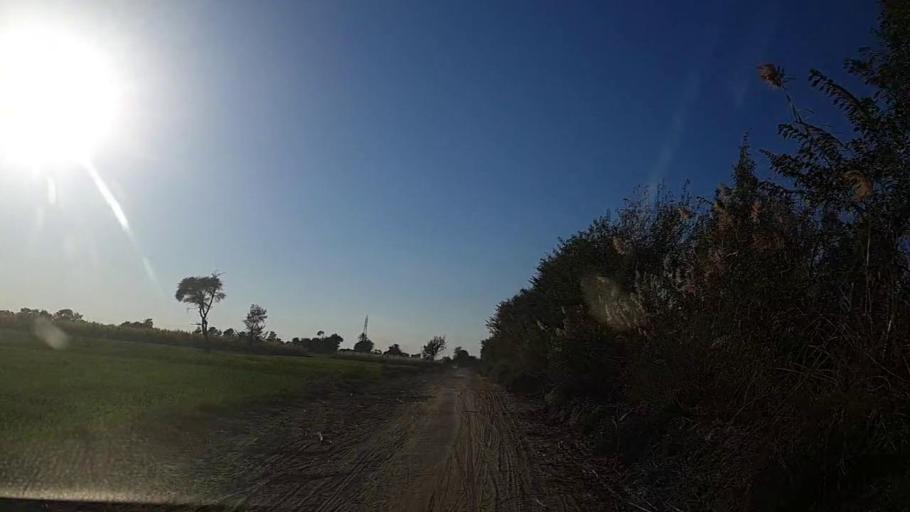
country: PK
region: Sindh
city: Sanghar
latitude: 26.1393
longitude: 68.9566
